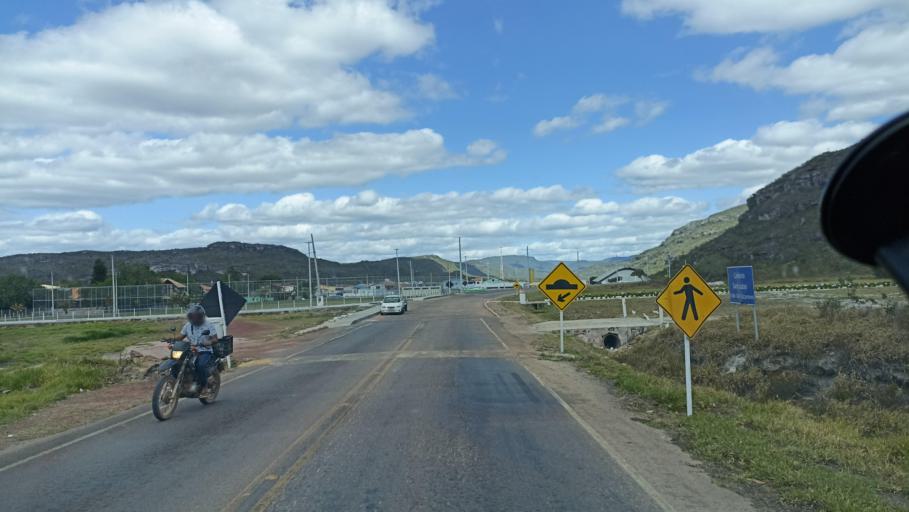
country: BR
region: Bahia
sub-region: Andarai
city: Vera Cruz
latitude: -13.0063
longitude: -41.3766
